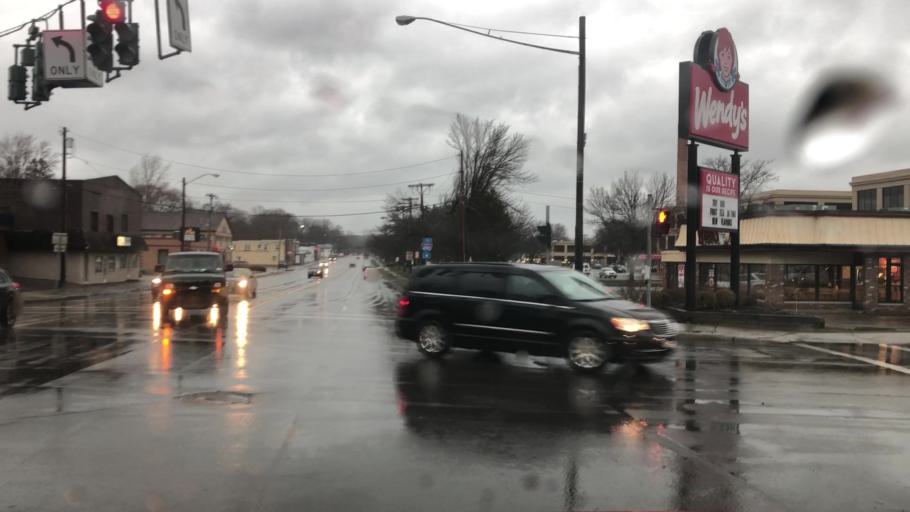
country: US
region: New York
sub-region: Monroe County
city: East Rochester
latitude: 43.1144
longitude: -77.4903
